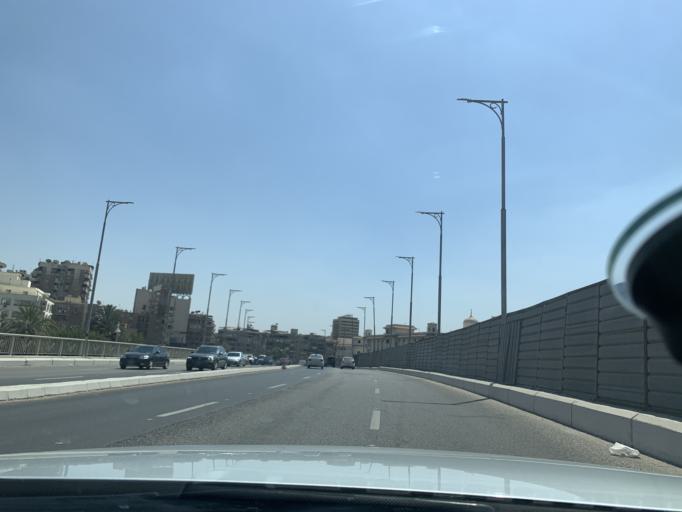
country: EG
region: Muhafazat al Qahirah
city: Cairo
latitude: 30.0873
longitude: 31.3352
